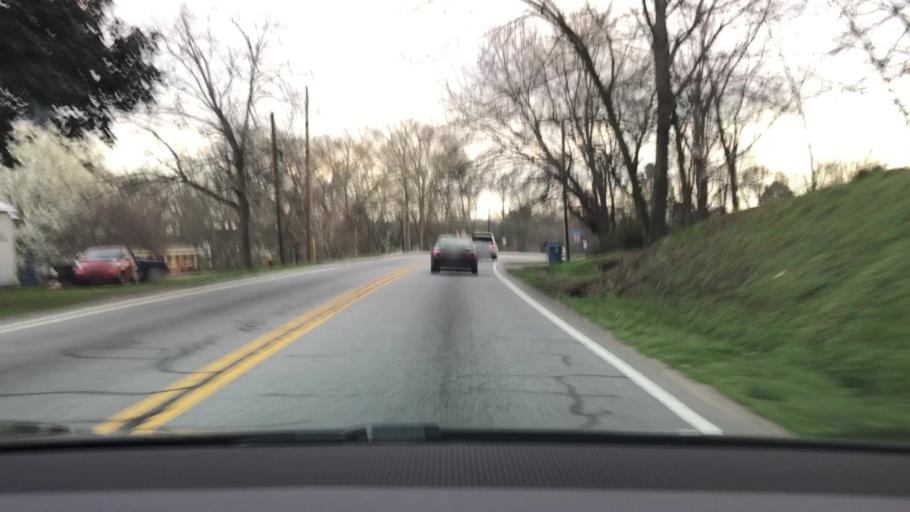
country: US
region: Georgia
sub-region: Barrow County
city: Russell
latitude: 33.9305
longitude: -83.7138
